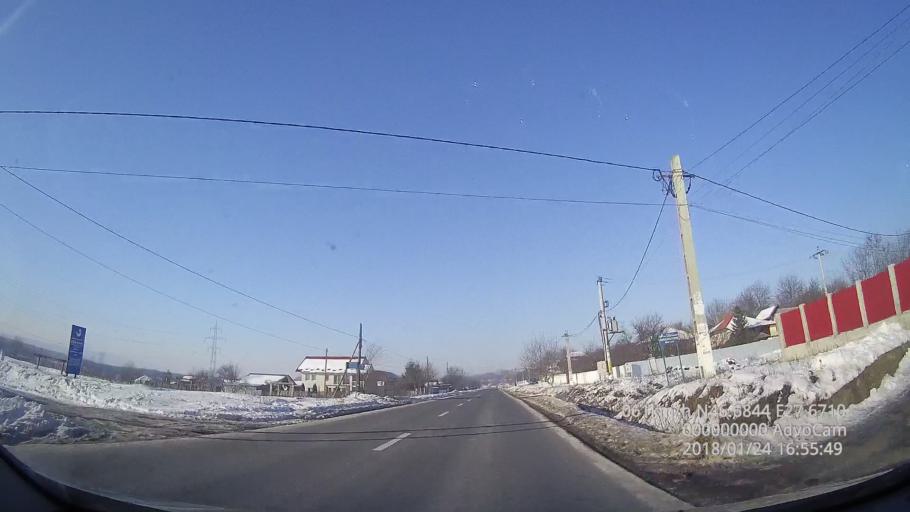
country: RO
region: Vaslui
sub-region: Municipiul Vaslui
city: Brodoc
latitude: 46.6848
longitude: 27.6709
